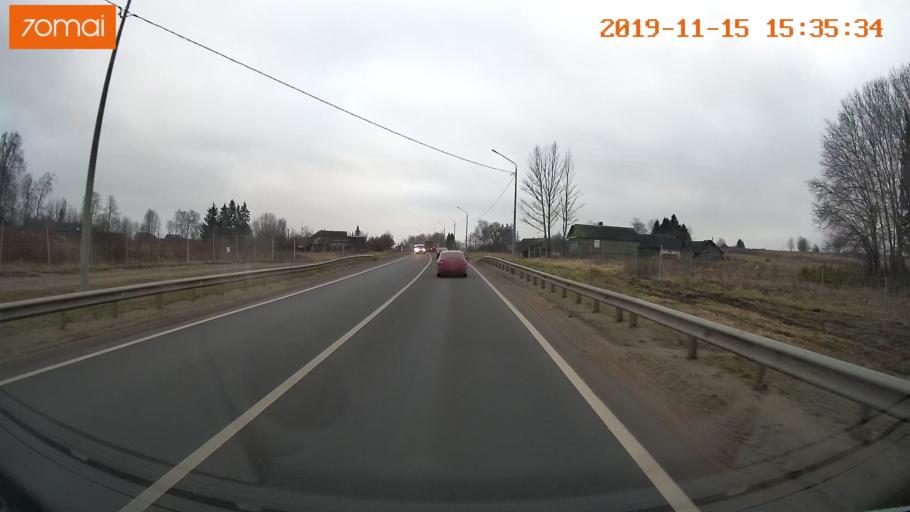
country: RU
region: Jaroslavl
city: Danilov
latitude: 58.0577
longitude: 40.0873
